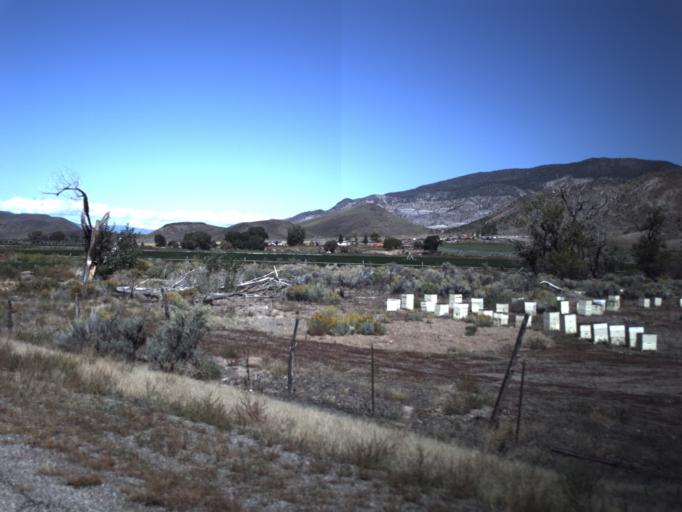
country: US
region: Utah
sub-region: Piute County
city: Junction
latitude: 38.2072
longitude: -112.1813
